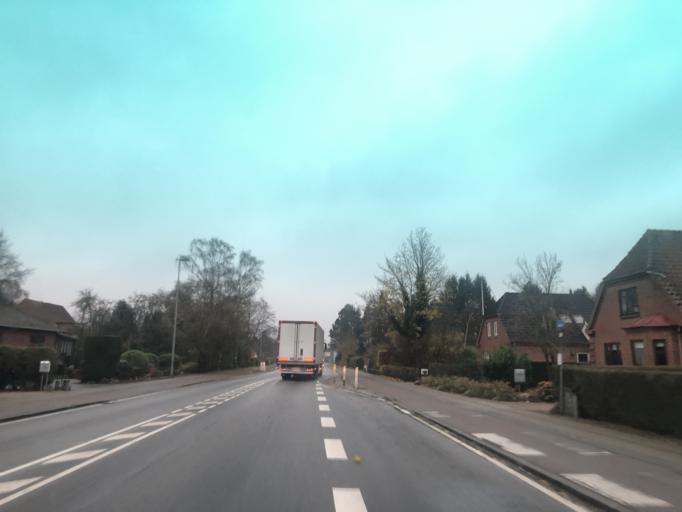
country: DK
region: South Denmark
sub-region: Nyborg Kommune
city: Ullerslev
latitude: 55.2616
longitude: 10.6739
